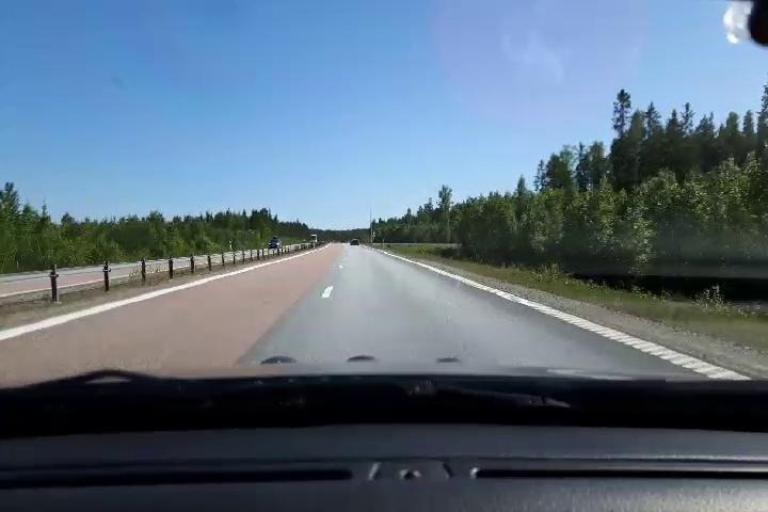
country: SE
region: Gaevleborg
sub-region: Soderhamns Kommun
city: Soderhamn
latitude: 61.4150
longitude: 16.9891
